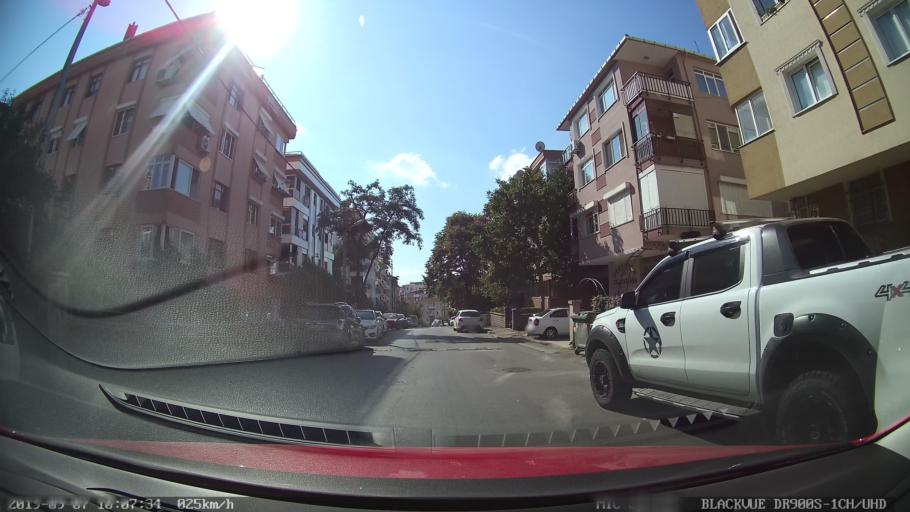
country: TR
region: Istanbul
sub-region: Atasehir
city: Atasehir
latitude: 40.9496
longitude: 29.1118
